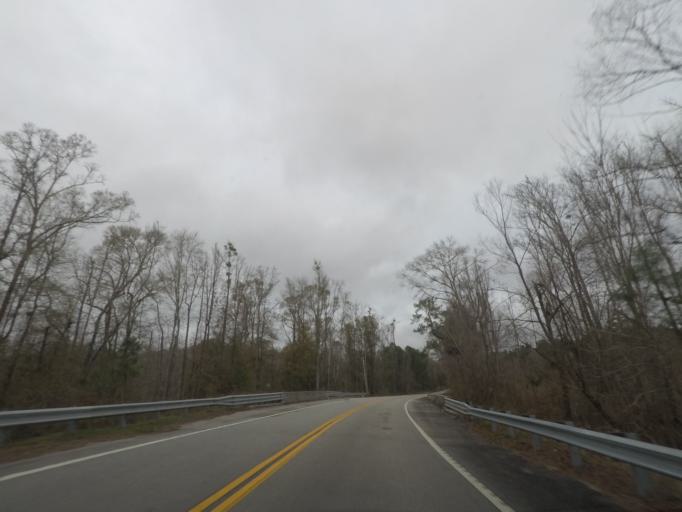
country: US
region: South Carolina
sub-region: Colleton County
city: Walterboro
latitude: 32.8930
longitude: -80.5170
